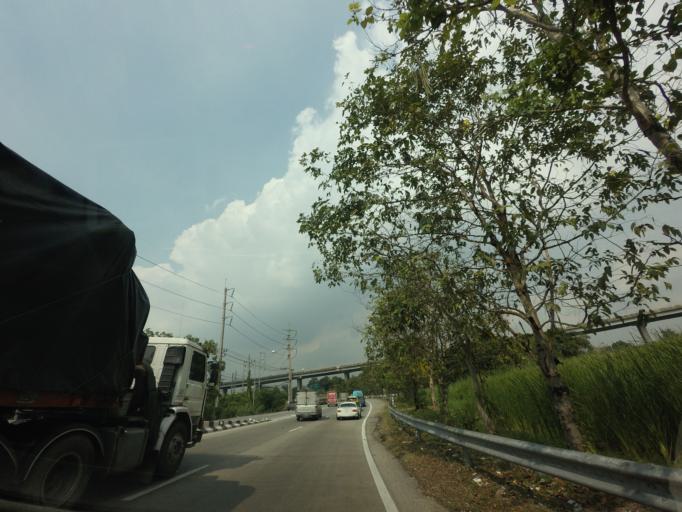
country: TH
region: Bangkok
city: Taling Chan
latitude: 13.7819
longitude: 100.4063
